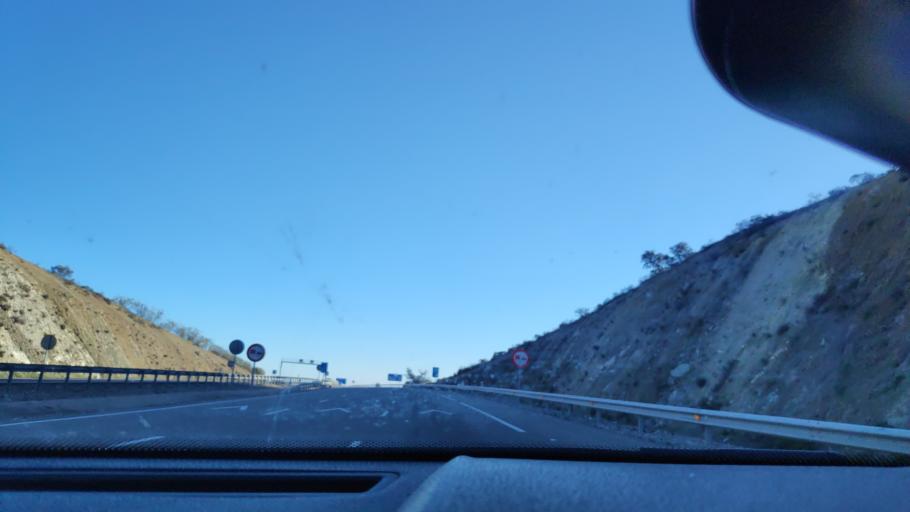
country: ES
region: Andalusia
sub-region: Provincia de Sevilla
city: El Ronquillo
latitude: 37.6395
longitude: -6.1550
